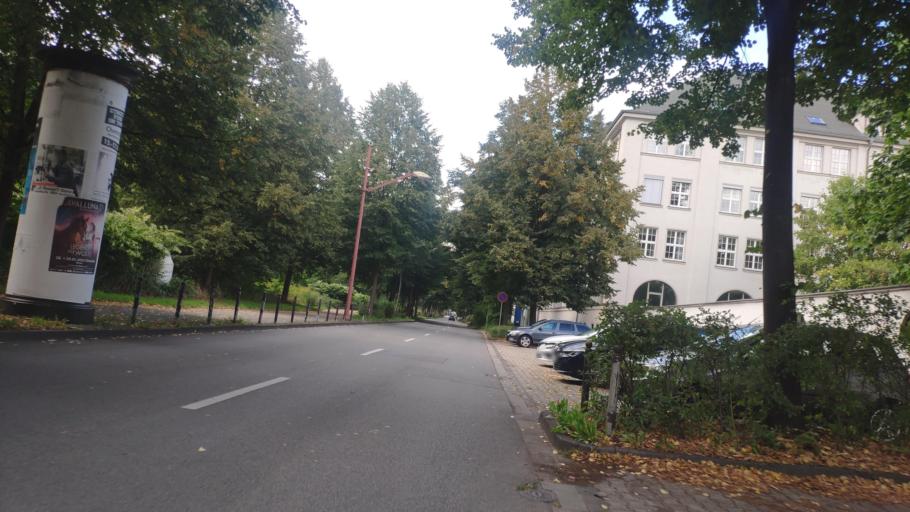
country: DE
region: Saxony
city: Chemnitz
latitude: 50.8104
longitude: 12.9046
